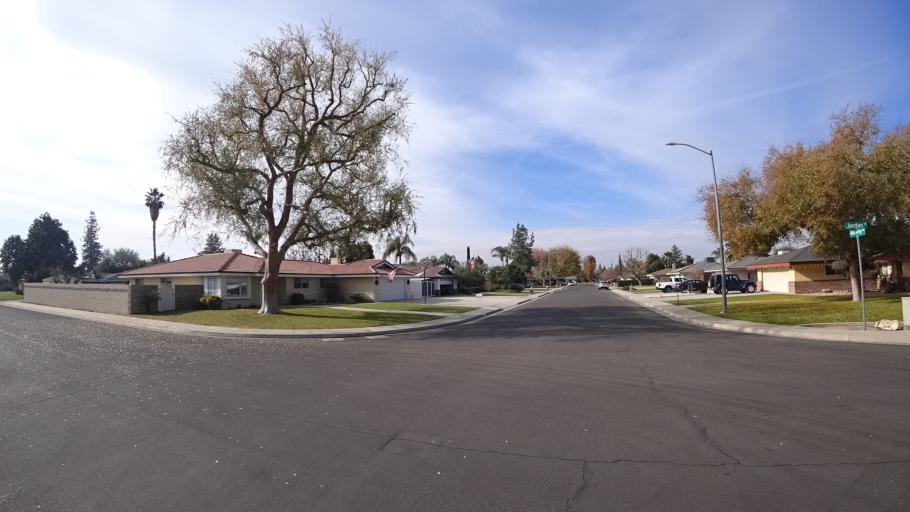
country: US
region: California
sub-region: Kern County
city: Greenacres
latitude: 35.4104
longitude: -119.0789
